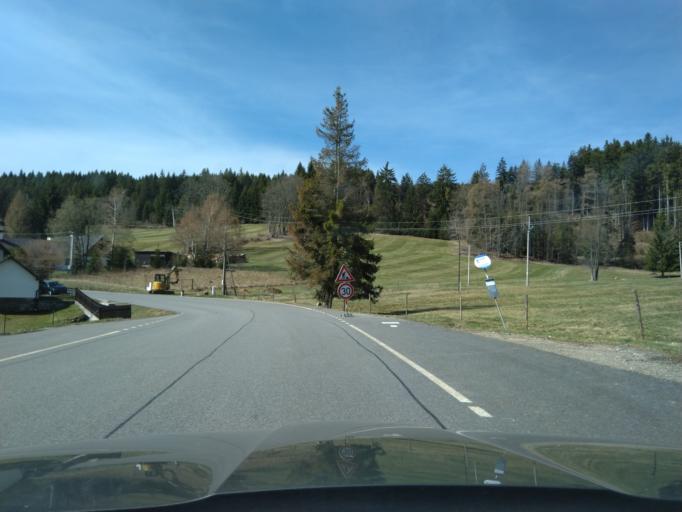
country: CZ
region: Jihocesky
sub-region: Okres Prachatice
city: Stachy
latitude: 49.0787
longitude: 13.6350
